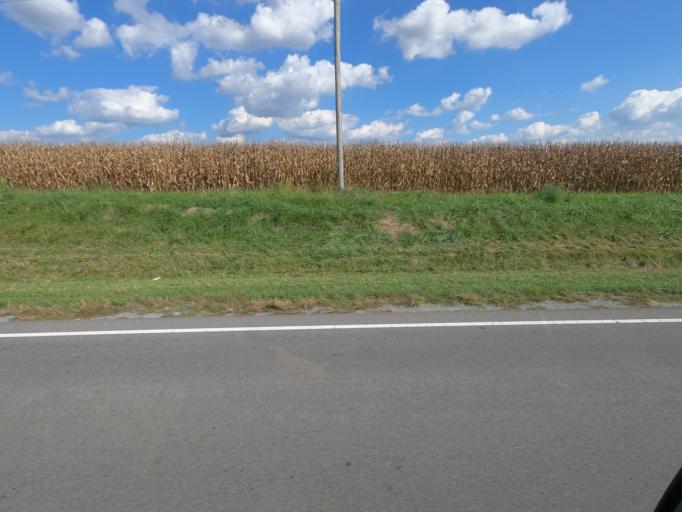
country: US
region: Illinois
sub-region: Massac County
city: Metropolis
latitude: 37.1856
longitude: -88.6766
